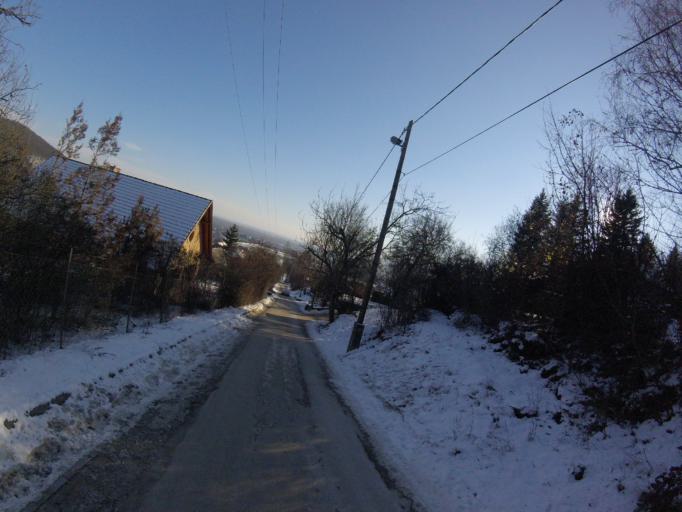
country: HU
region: Pest
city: Kismaros
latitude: 47.8340
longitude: 18.9998
